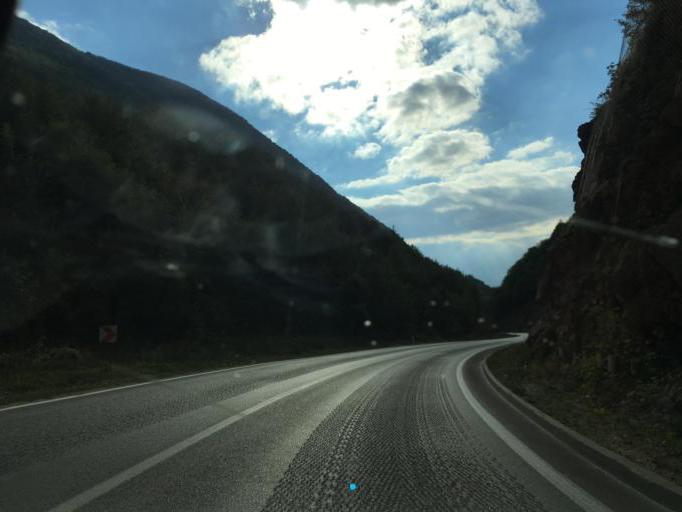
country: BA
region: Federation of Bosnia and Herzegovina
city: Bugojno
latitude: 44.0874
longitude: 17.5493
